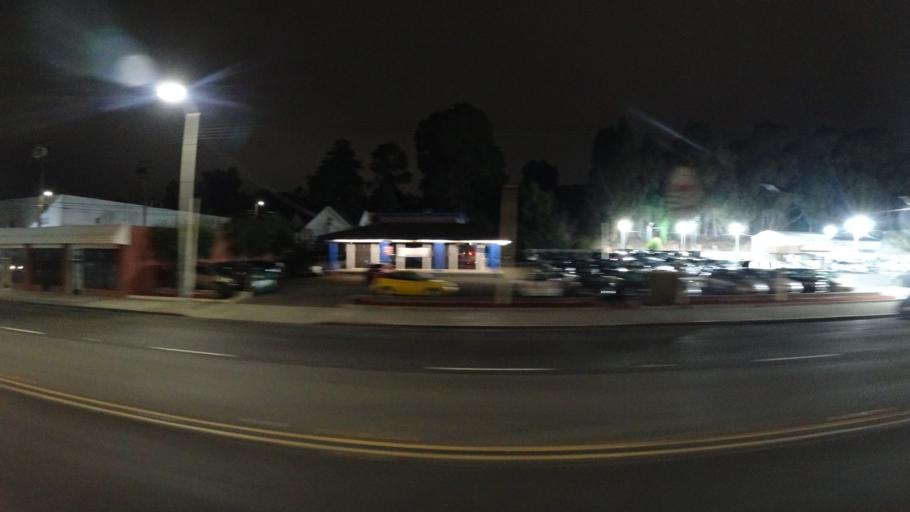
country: US
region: California
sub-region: Alameda County
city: Hayward
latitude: 37.6761
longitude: -122.0889
